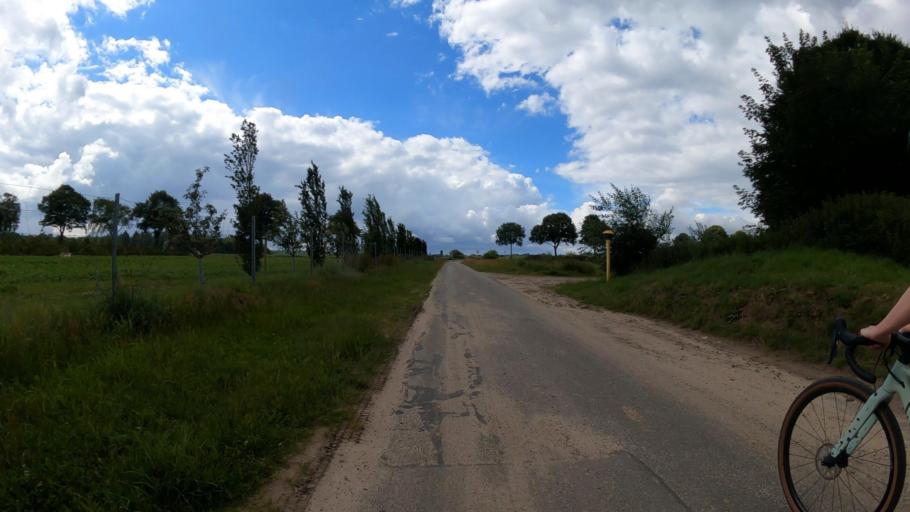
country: DE
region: Lower Saxony
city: Seevetal
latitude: 53.4346
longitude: 9.9131
